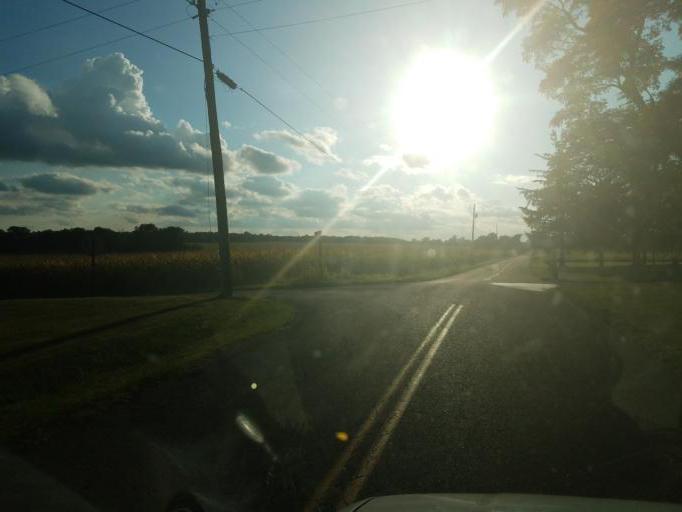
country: US
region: Ohio
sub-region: Knox County
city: Fredericktown
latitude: 40.4244
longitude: -82.6052
